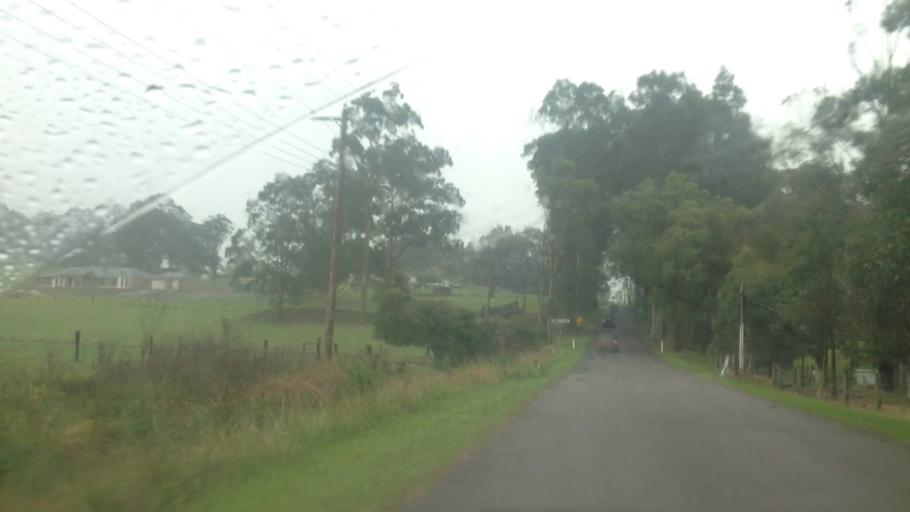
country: AU
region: New South Wales
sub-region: Wyong Shire
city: Little Jilliby
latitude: -33.2034
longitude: 151.3637
